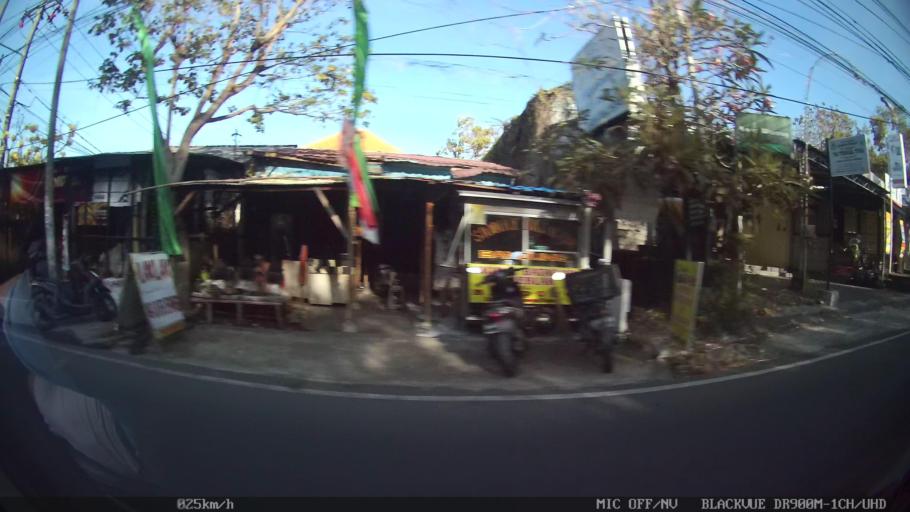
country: ID
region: Bali
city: Jimbaran
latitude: -8.7940
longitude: 115.1877
